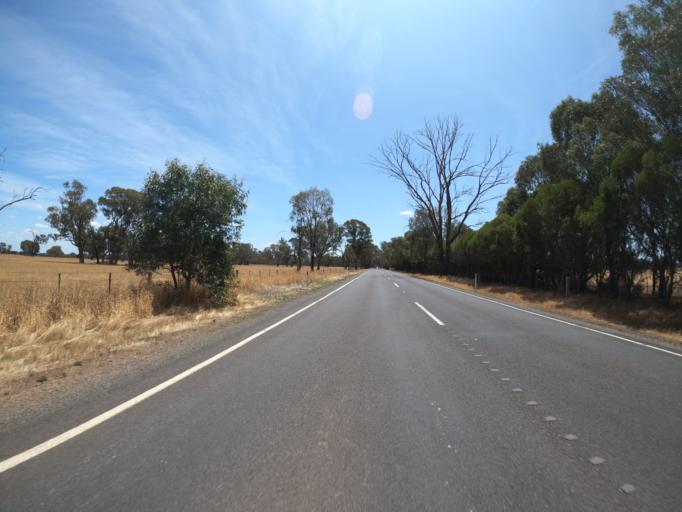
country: AU
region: Victoria
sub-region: Benalla
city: Benalla
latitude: -36.5064
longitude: 146.0257
